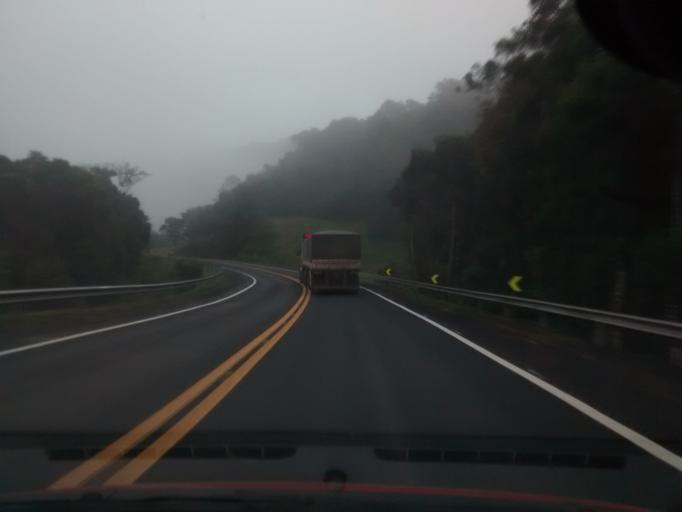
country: BR
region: Rio Grande do Sul
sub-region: Vacaria
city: Estrela
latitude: -28.1952
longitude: -50.7366
